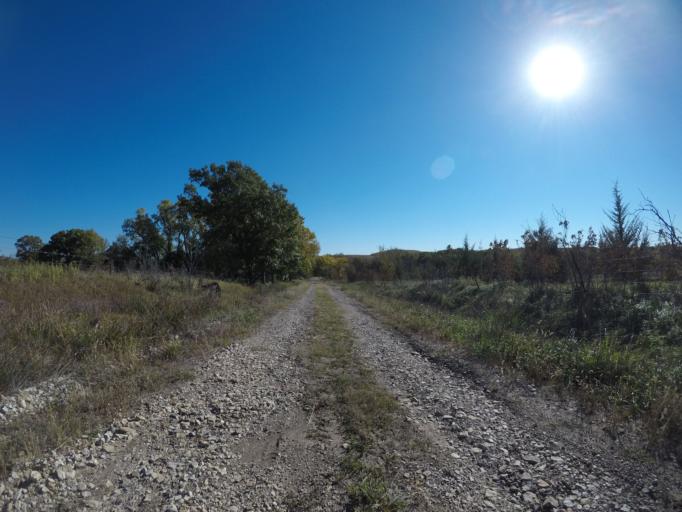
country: US
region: Kansas
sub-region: Wabaunsee County
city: Alma
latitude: 38.8841
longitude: -96.3827
